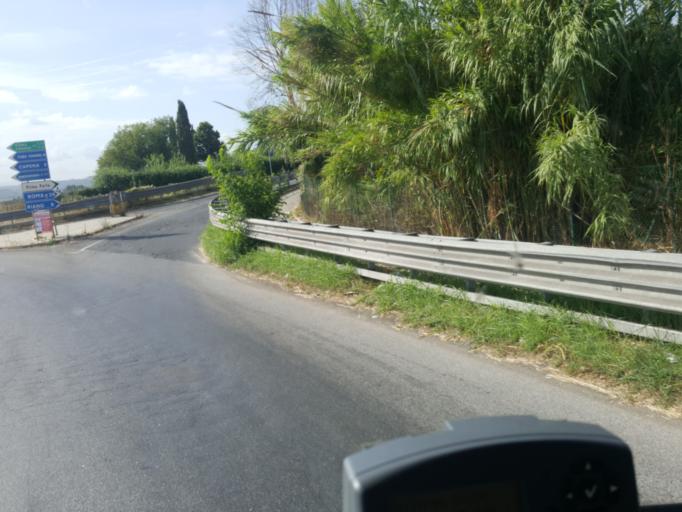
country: IT
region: Latium
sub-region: Citta metropolitana di Roma Capitale
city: Girardi-Bellavista-Terrazze
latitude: 42.0943
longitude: 12.5653
